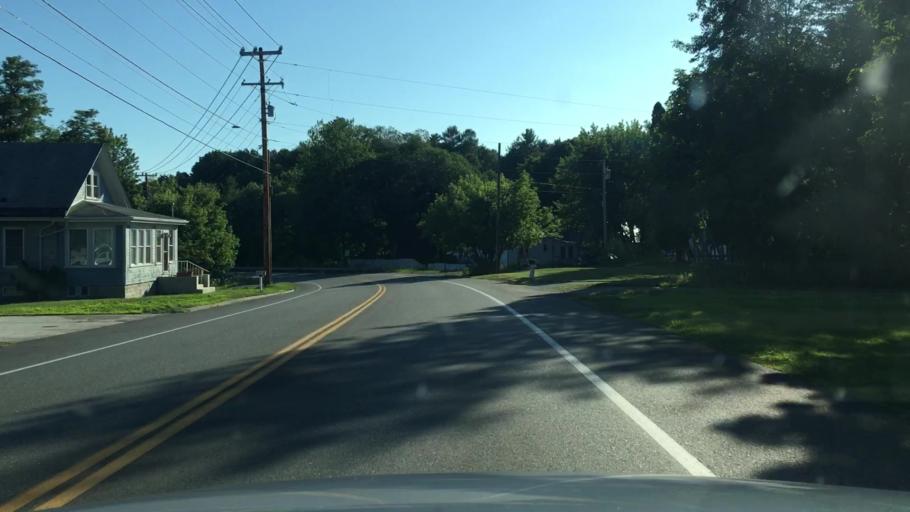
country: US
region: Maine
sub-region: Penobscot County
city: Veazie
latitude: 44.8192
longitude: -68.7290
